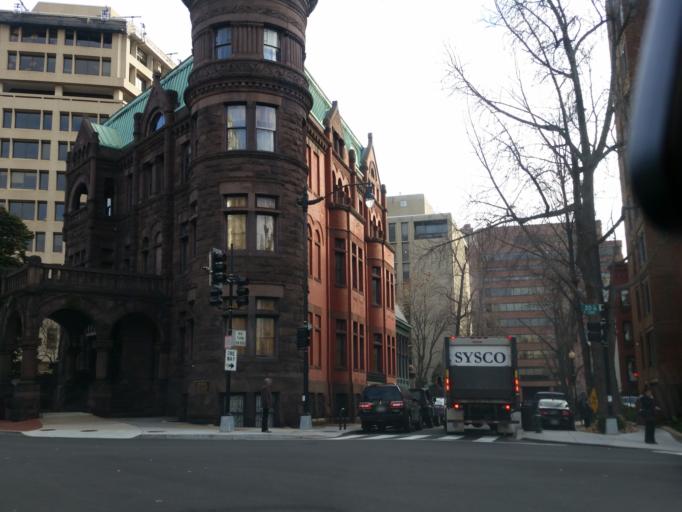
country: US
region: Washington, D.C.
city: Washington, D.C.
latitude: 38.9079
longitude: -77.0451
